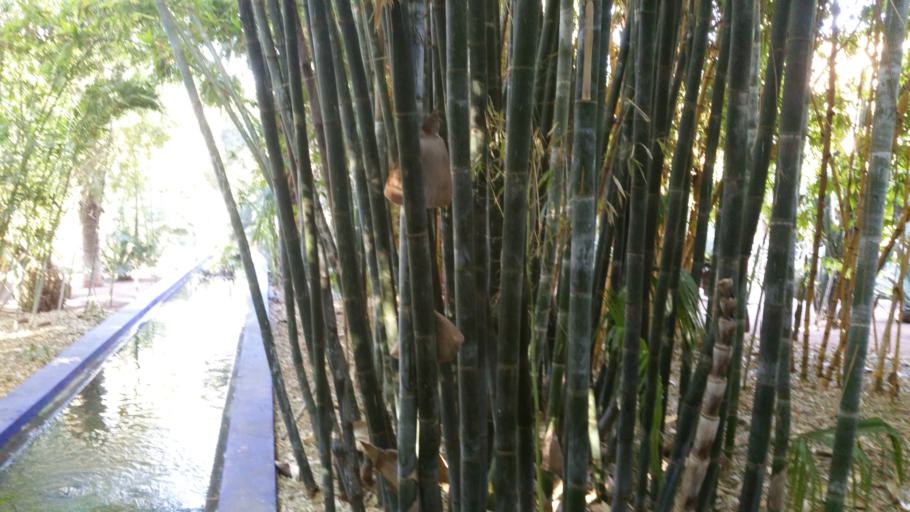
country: MA
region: Marrakech-Tensift-Al Haouz
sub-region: Marrakech
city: Marrakesh
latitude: 31.6413
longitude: -8.0025
